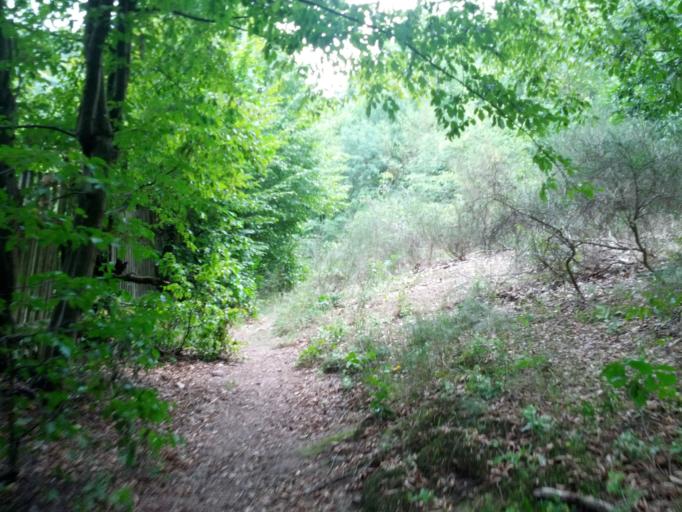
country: DE
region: Thuringia
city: Eisenach
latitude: 50.9732
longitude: 10.2993
